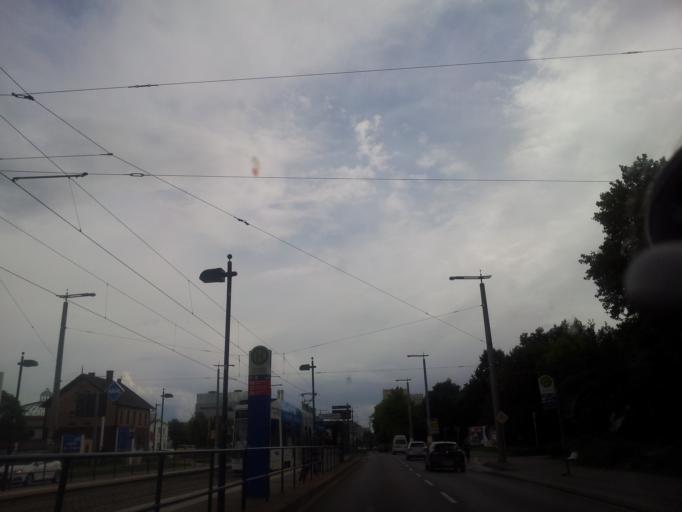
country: DE
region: Saxony
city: Leipzig
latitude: 51.3562
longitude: 12.3768
